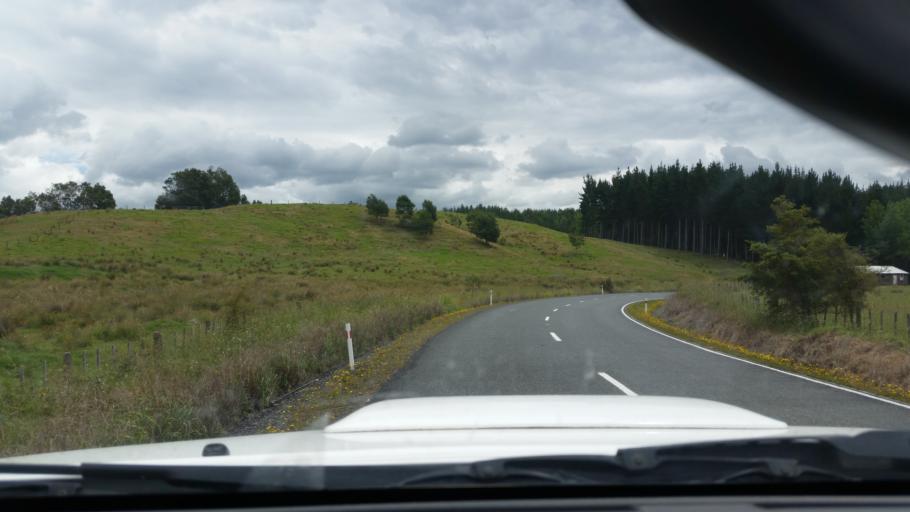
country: NZ
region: Northland
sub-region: Kaipara District
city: Dargaville
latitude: -35.7498
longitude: 173.8808
